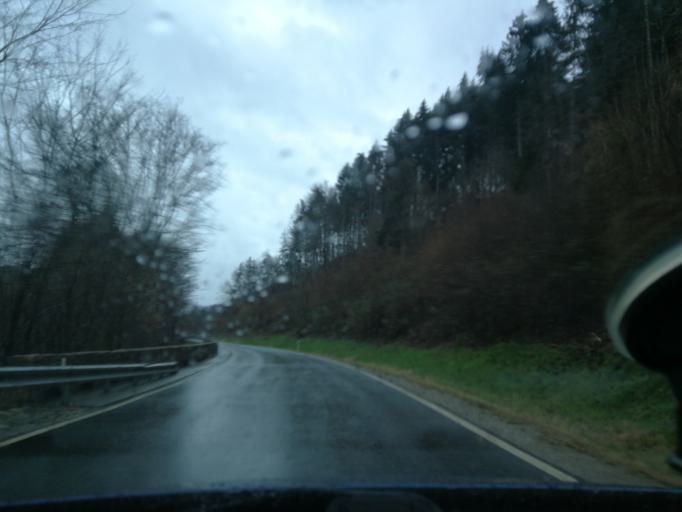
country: DE
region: Rheinland-Pfalz
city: Berglicht
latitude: 49.8122
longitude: 6.9567
